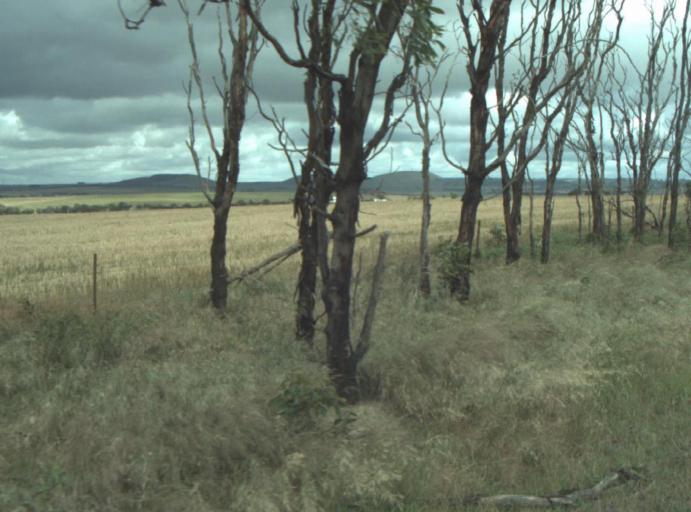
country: AU
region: Victoria
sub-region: Greater Geelong
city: Lara
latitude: -37.8936
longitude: 144.3823
